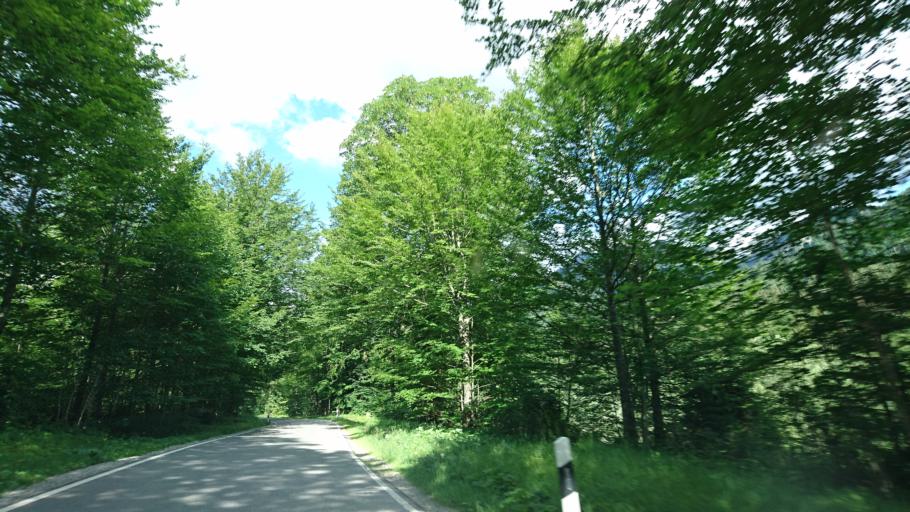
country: DE
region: Bavaria
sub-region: Upper Bavaria
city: Unterammergau
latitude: 47.5661
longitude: 10.9472
